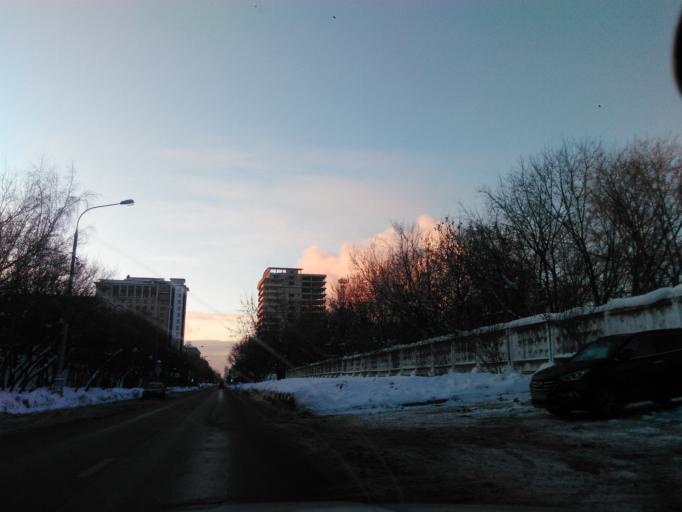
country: RU
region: Moscow
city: Sokol
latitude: 55.7910
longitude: 37.5069
